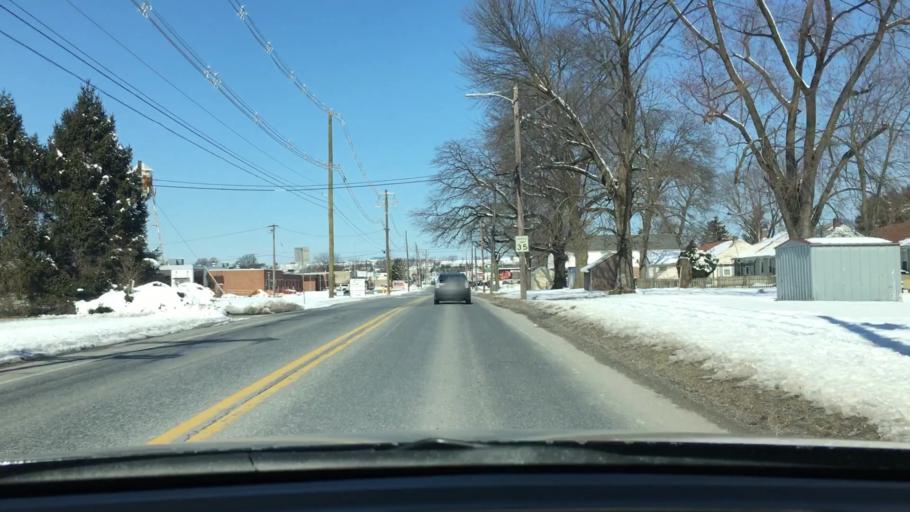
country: US
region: Pennsylvania
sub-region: York County
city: West York
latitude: 39.9735
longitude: -76.7535
